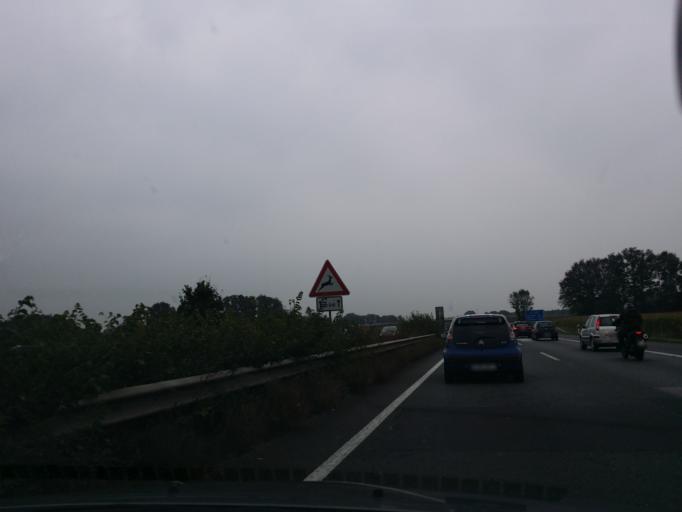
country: DE
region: Lower Saxony
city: Holdorf
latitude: 52.5921
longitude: 8.1116
